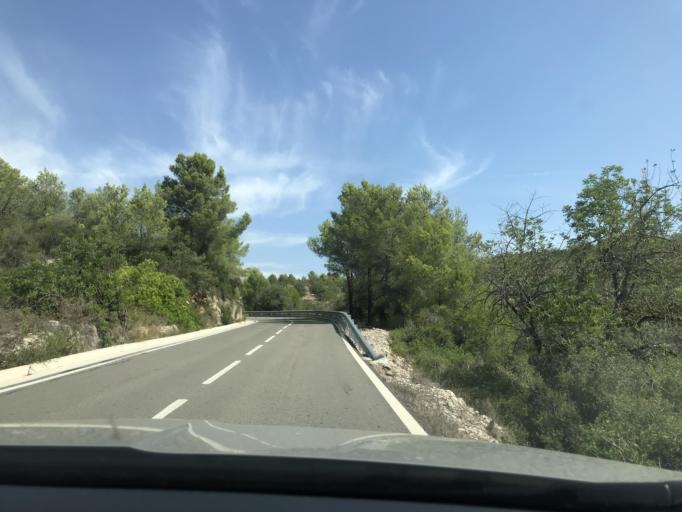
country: ES
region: Catalonia
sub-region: Provincia de Tarragona
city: Salomo
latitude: 41.2008
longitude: 1.3864
